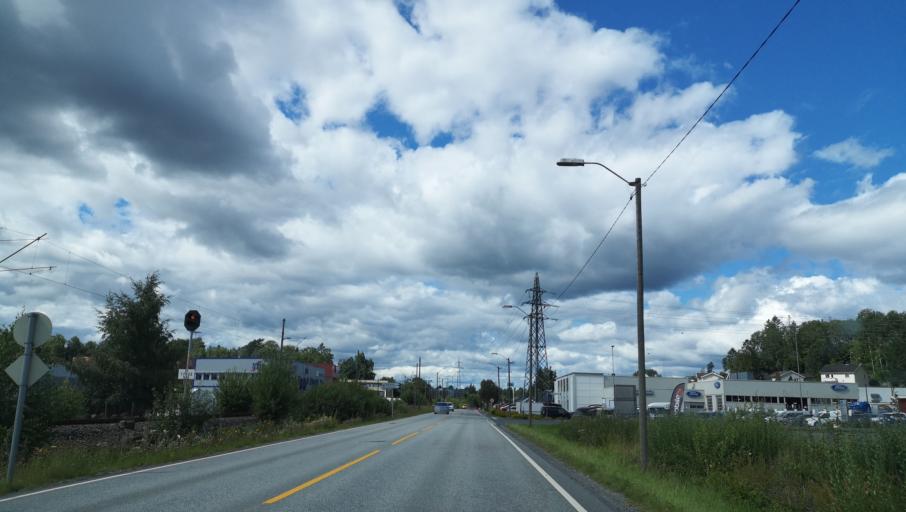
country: NO
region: Akershus
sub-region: Ski
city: Ski
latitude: 59.7133
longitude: 10.8517
